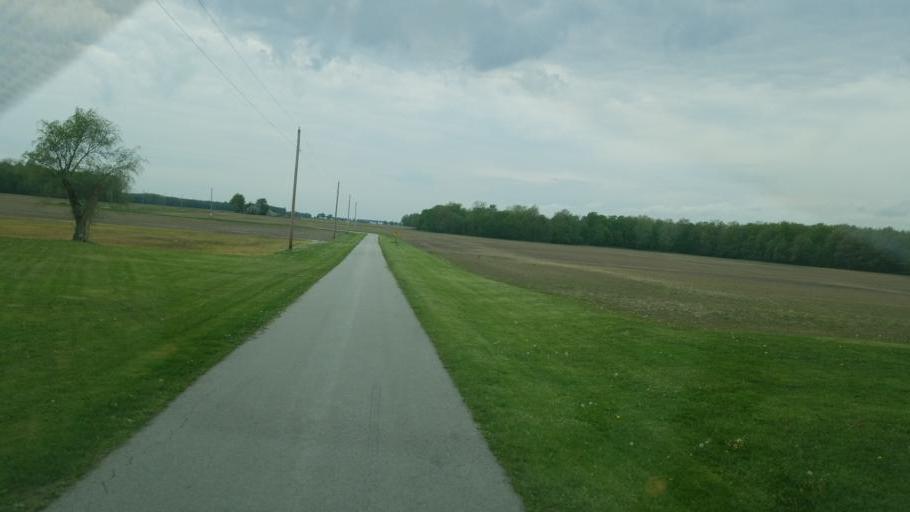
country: US
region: Ohio
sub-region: Huron County
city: Willard
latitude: 41.0196
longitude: -82.8447
